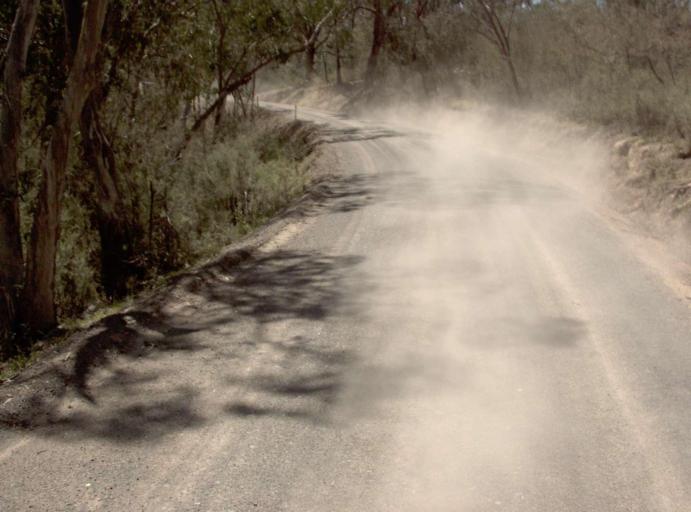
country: AU
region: New South Wales
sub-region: Bombala
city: Bombala
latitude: -37.1276
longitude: 148.6643
